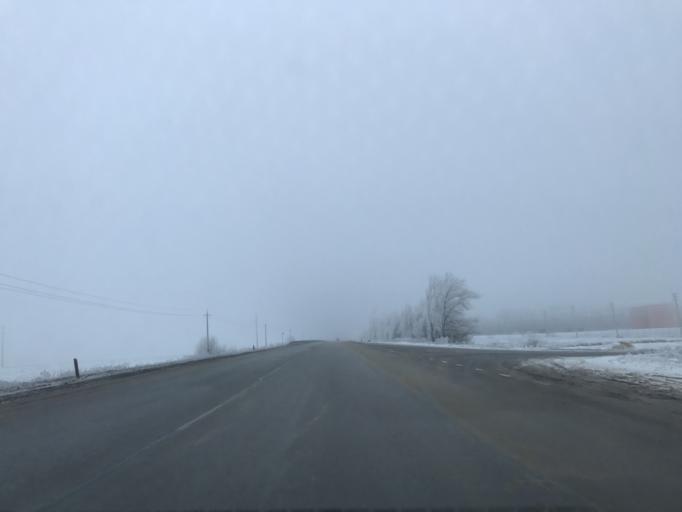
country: RU
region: Rostov
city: Grushevskaya
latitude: 47.3787
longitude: 39.8671
